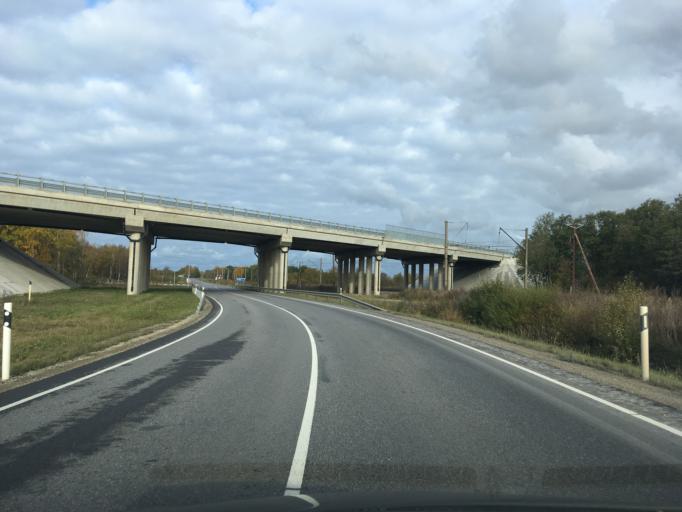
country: EE
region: Harju
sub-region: Joelaehtme vald
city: Loo
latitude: 59.4064
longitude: 24.9177
